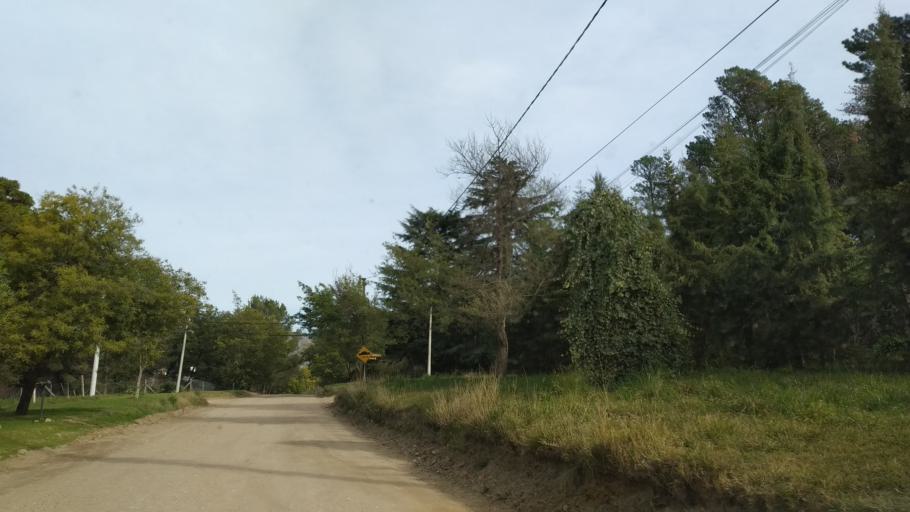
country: AR
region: Buenos Aires
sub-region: Partido de Tornquist
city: Tornquist
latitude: -38.0841
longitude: -61.9291
